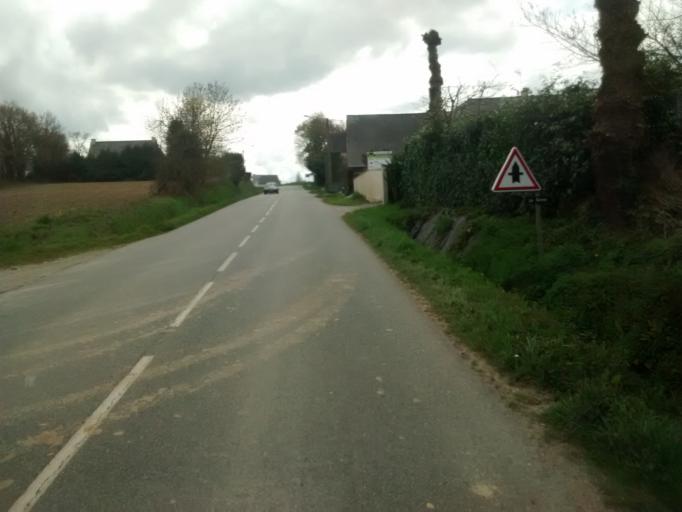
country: FR
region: Brittany
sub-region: Departement du Morbihan
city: Caro
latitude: 47.8835
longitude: -2.3589
